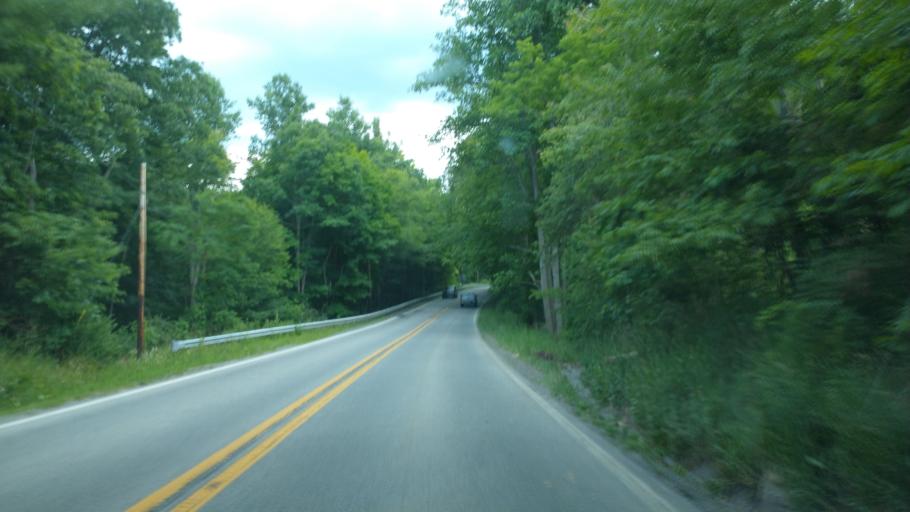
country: US
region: West Virginia
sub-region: Mercer County
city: Athens
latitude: 37.4443
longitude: -81.0013
